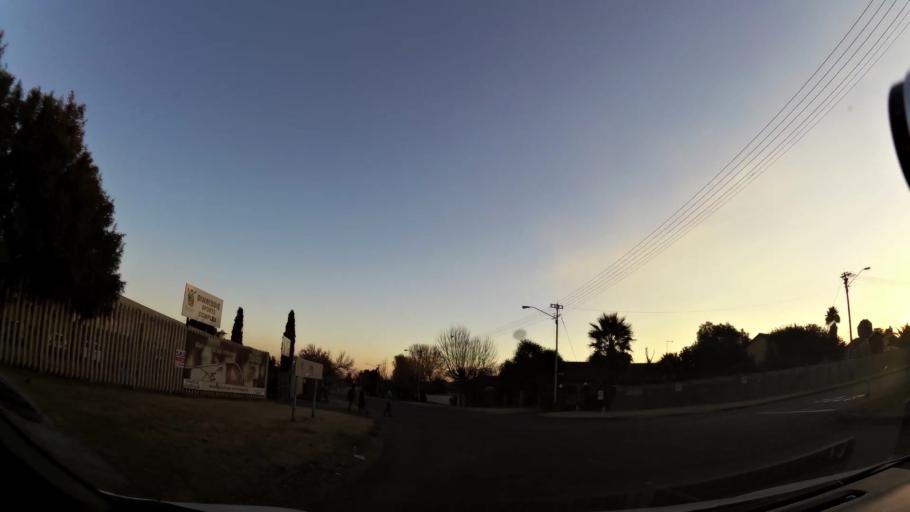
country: ZA
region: Gauteng
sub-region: Ekurhuleni Metropolitan Municipality
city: Germiston
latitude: -26.2706
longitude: 28.1578
